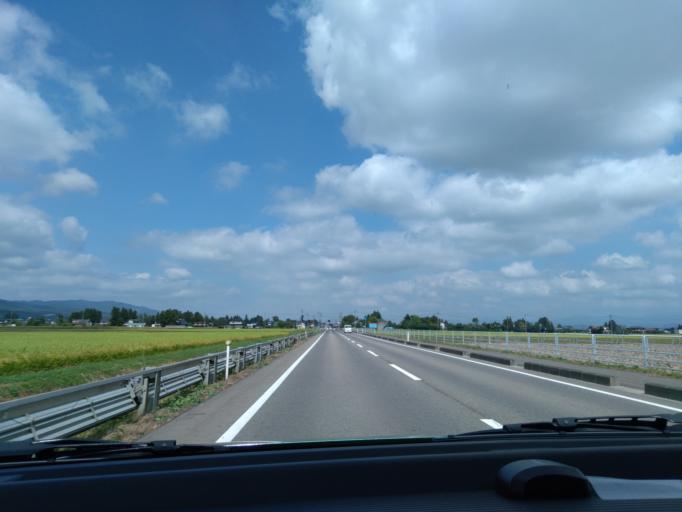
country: JP
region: Iwate
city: Hanamaki
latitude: 39.4382
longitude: 141.0971
